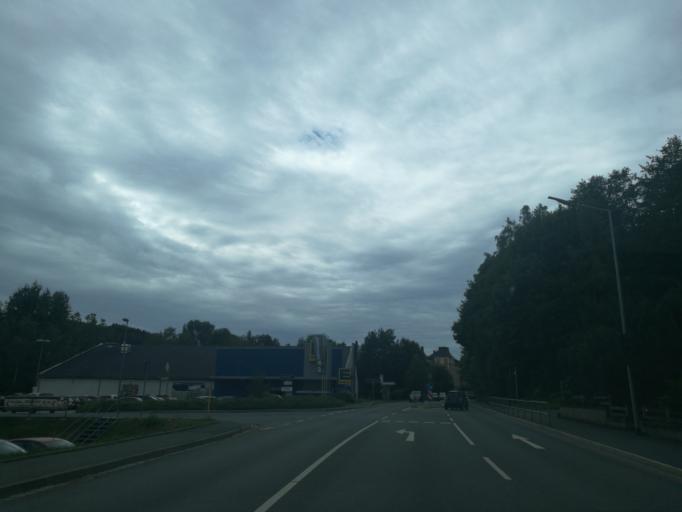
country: DE
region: Saxony
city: Adorf
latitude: 50.3156
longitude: 12.2556
